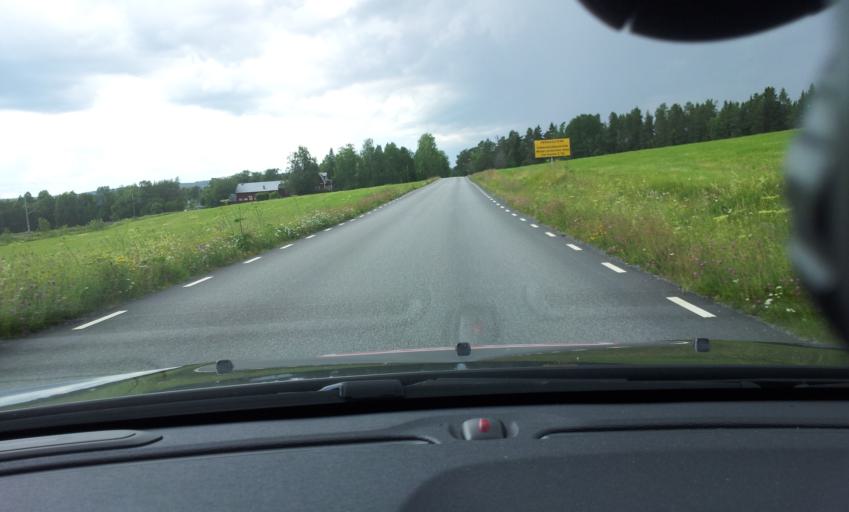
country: SE
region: Jaemtland
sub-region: Krokoms Kommun
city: Valla
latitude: 63.3258
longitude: 14.0369
